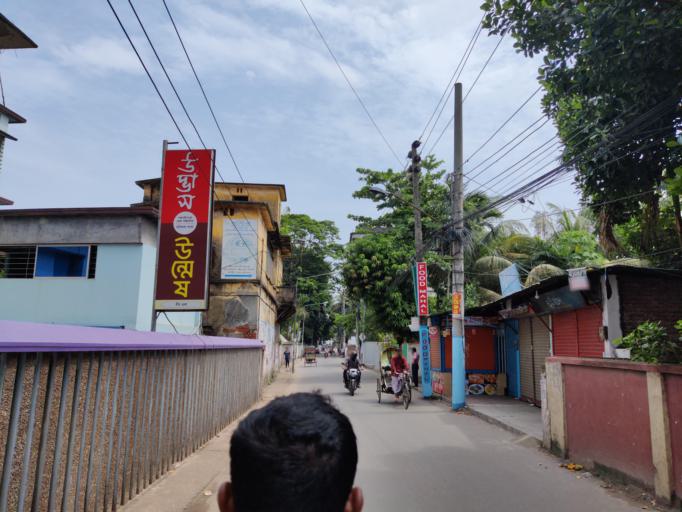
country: BD
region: Barisal
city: Barisal
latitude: 22.7029
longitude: 90.3652
